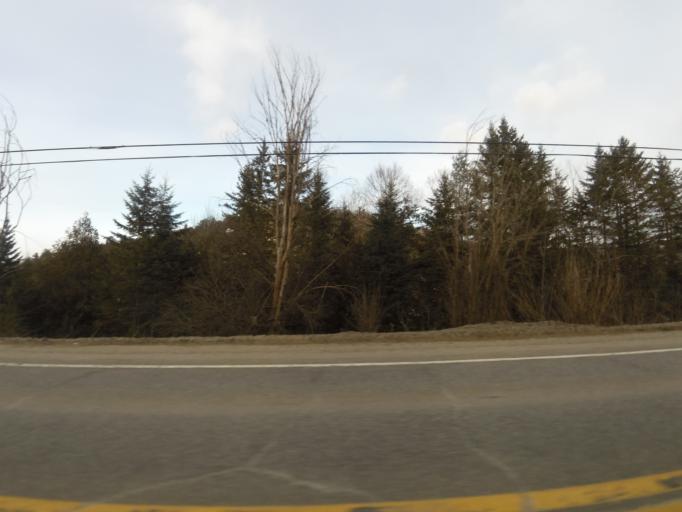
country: CA
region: Quebec
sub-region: Outaouais
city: Wakefield
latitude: 45.7677
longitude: -75.9345
